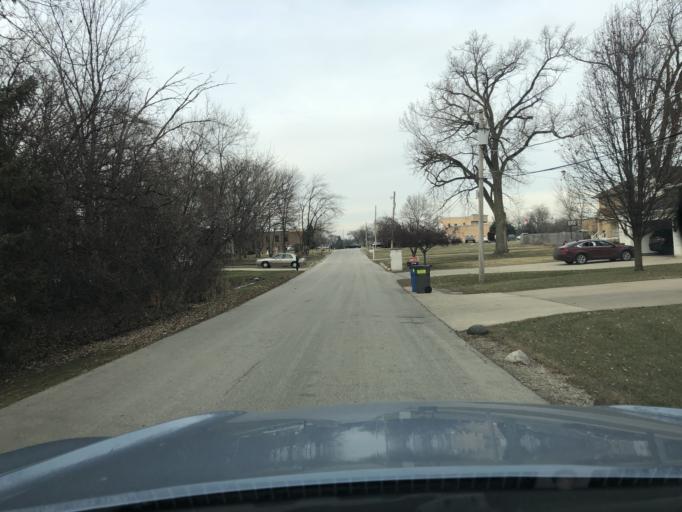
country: US
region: Illinois
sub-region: DuPage County
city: Addison
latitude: 41.9400
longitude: -88.0118
